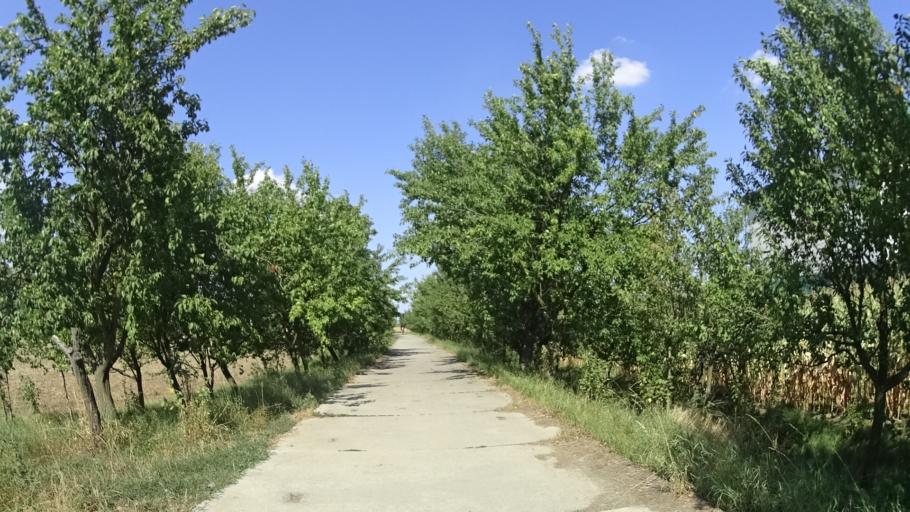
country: CZ
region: Zlin
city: Uhersky Ostroh
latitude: 48.9941
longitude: 17.4026
